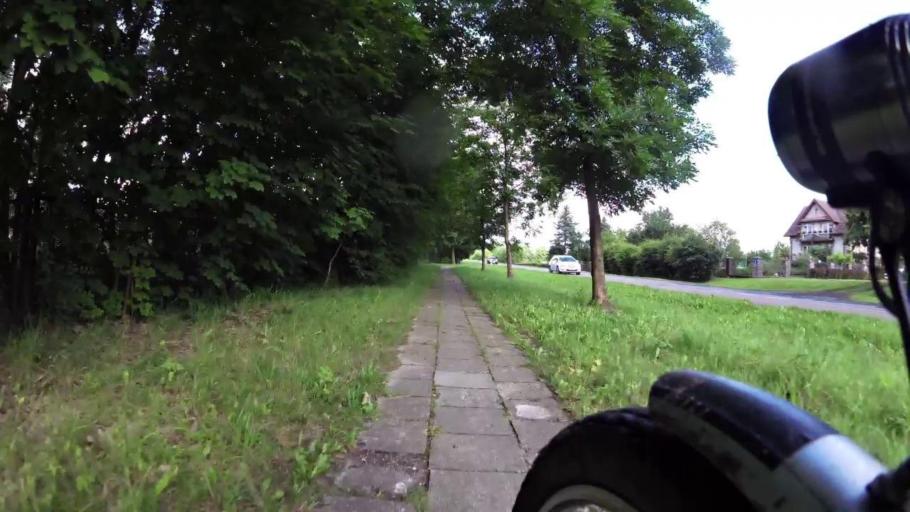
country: PL
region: West Pomeranian Voivodeship
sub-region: Powiat swidwinski
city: Swidwin
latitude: 53.7758
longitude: 15.8385
